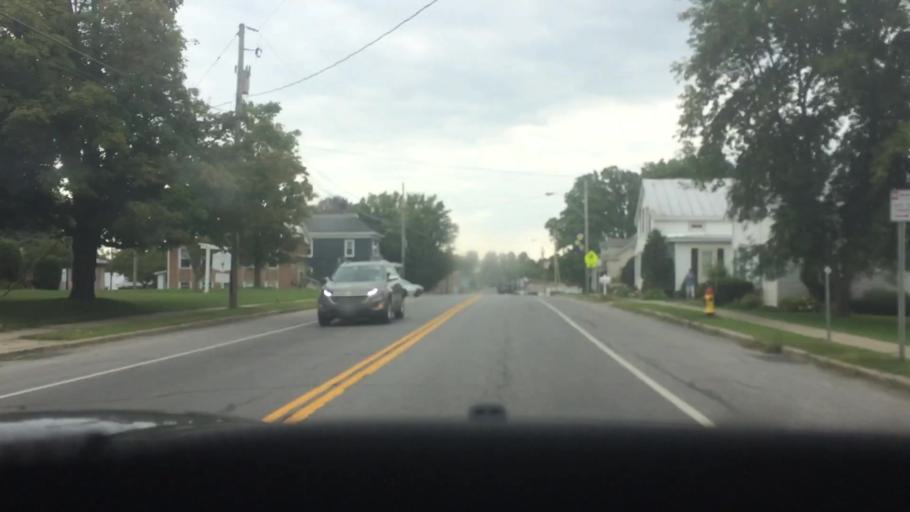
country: US
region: New York
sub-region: St. Lawrence County
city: Ogdensburg
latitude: 44.6190
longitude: -75.4089
